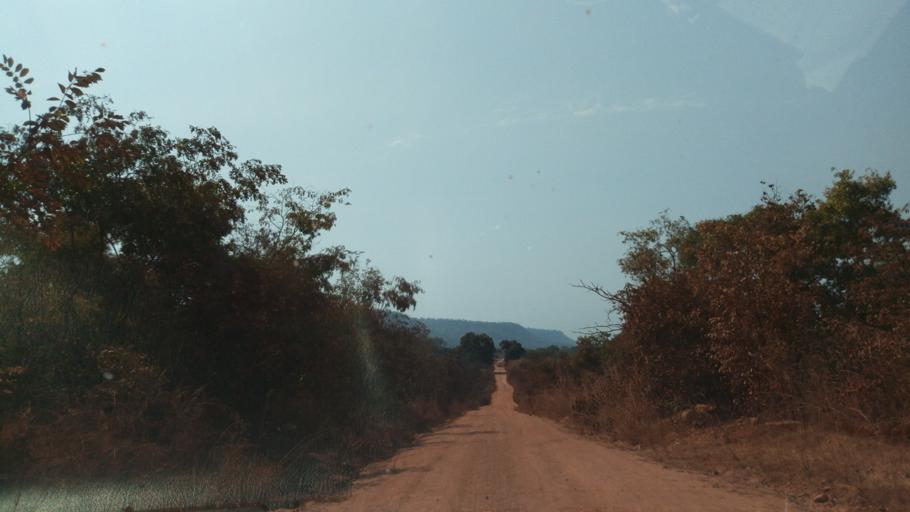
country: ZM
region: Luapula
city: Nchelenge
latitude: -8.5915
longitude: 28.7869
